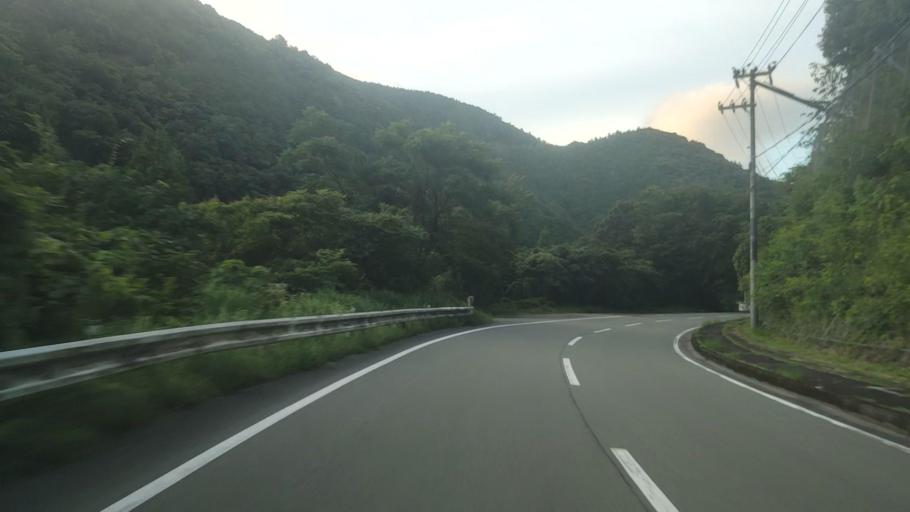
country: JP
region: Wakayama
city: Shingu
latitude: 33.8194
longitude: 135.7680
